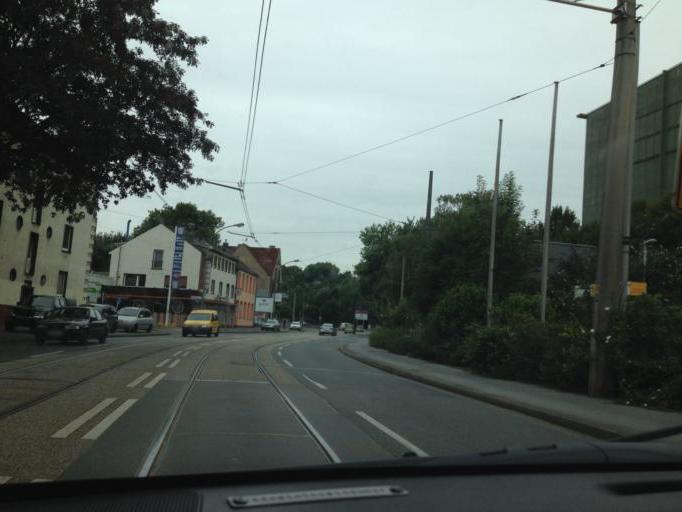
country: DE
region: North Rhine-Westphalia
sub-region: Regierungsbezirk Arnsberg
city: Dortmund
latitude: 51.5117
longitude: 7.4303
